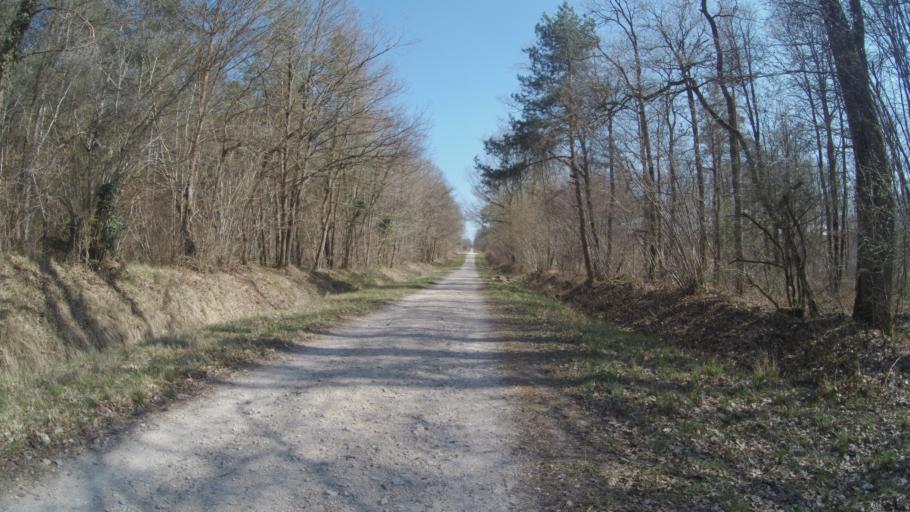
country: FR
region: Centre
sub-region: Departement du Loiret
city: Chanteau
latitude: 47.9500
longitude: 1.9608
